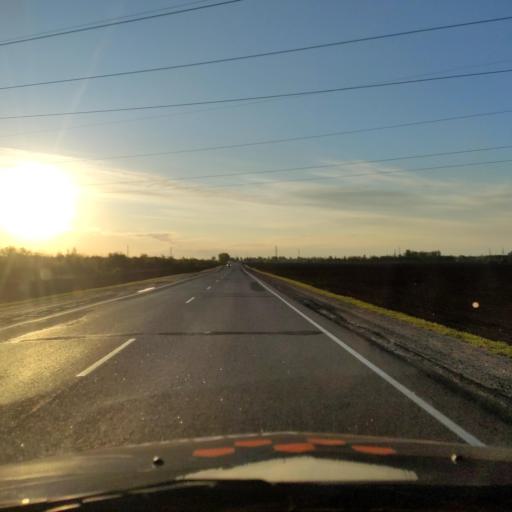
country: RU
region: Orjol
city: Livny
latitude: 52.4407
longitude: 37.5563
